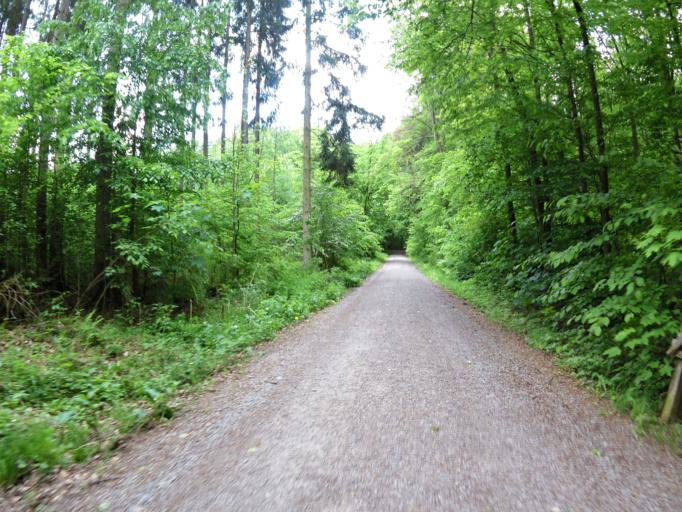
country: DE
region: Bavaria
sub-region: Regierungsbezirk Unterfranken
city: Kist
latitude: 49.7372
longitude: 9.8551
